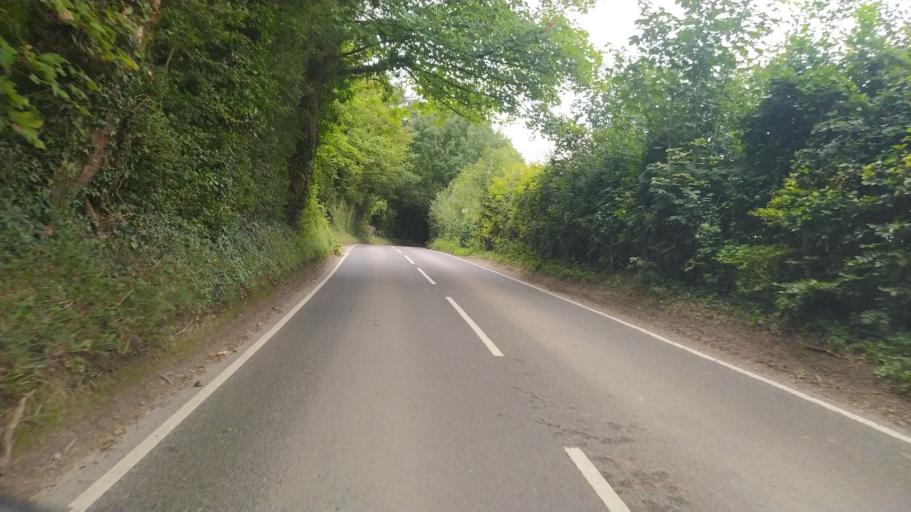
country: GB
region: England
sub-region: Dorset
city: Dorchester
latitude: 50.7552
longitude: -2.3785
